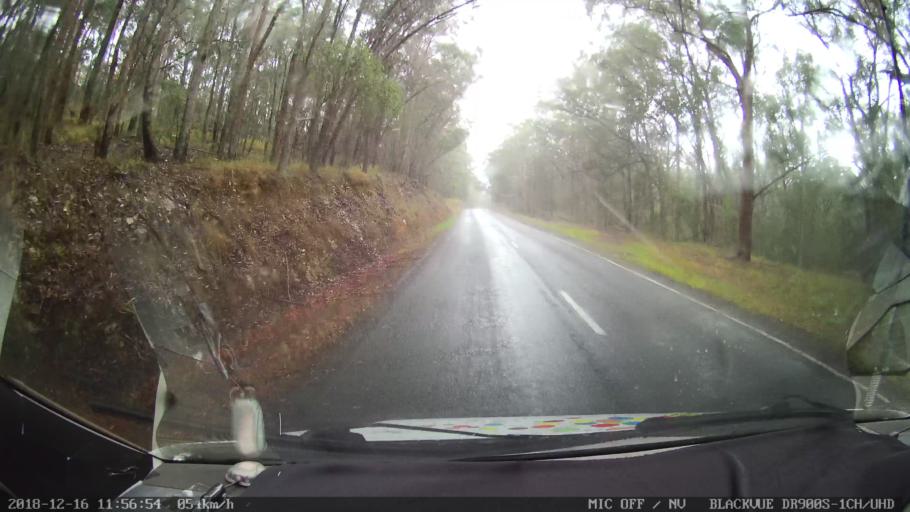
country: AU
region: New South Wales
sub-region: Tenterfield Municipality
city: Carrolls Creek
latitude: -28.9167
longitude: 152.3024
